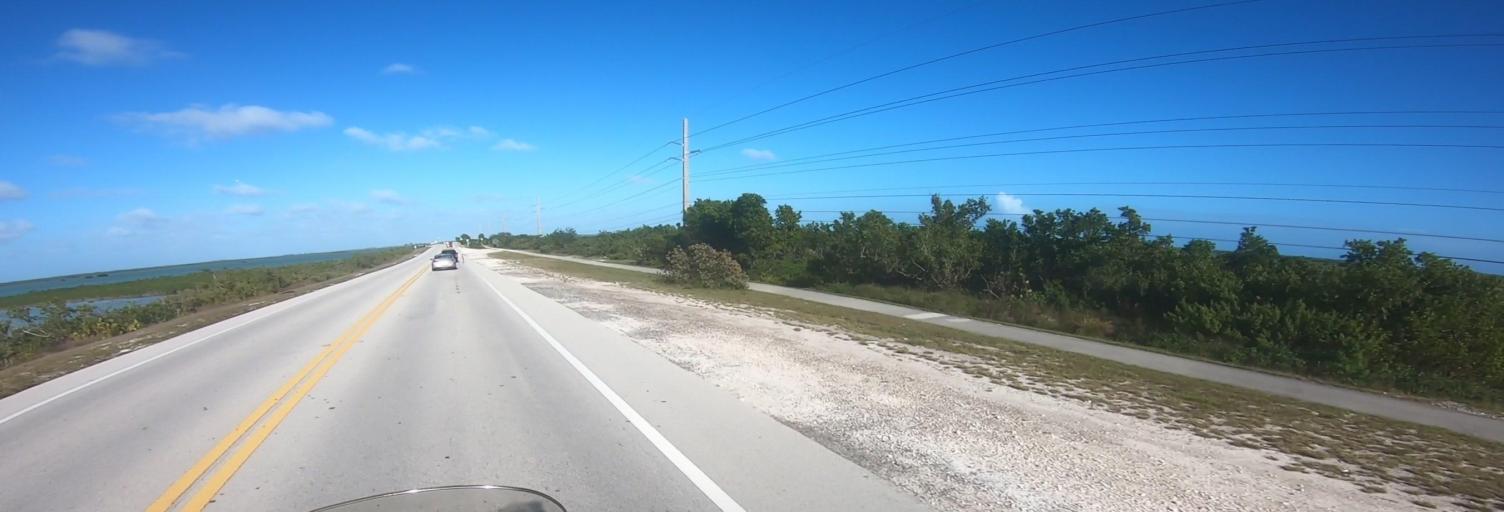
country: US
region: Florida
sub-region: Monroe County
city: Big Coppitt Key
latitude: 24.6132
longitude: -81.6220
